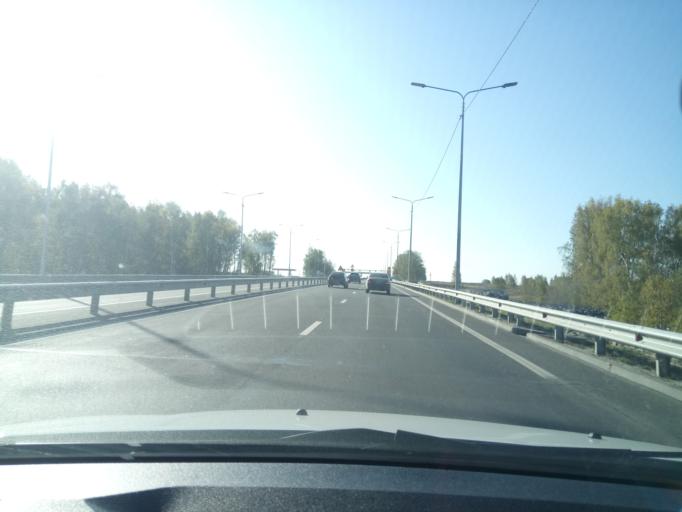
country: RU
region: Nizjnij Novgorod
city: Burevestnik
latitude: 56.0044
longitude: 43.9676
